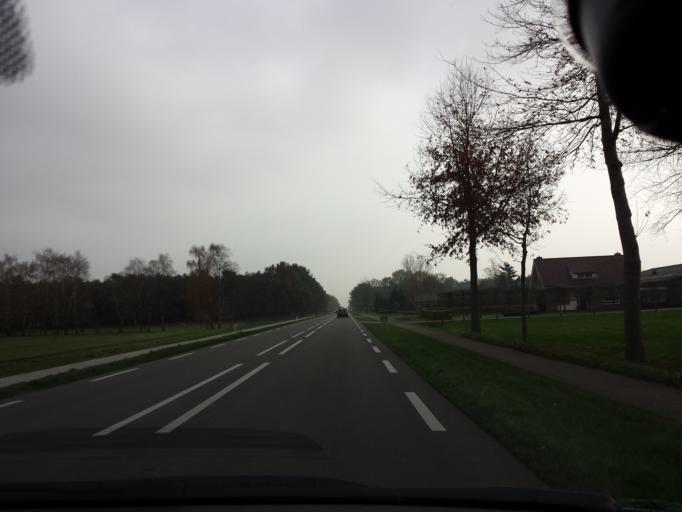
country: NL
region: Limburg
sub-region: Gemeente Venray
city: Venray
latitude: 51.4833
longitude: 5.9089
